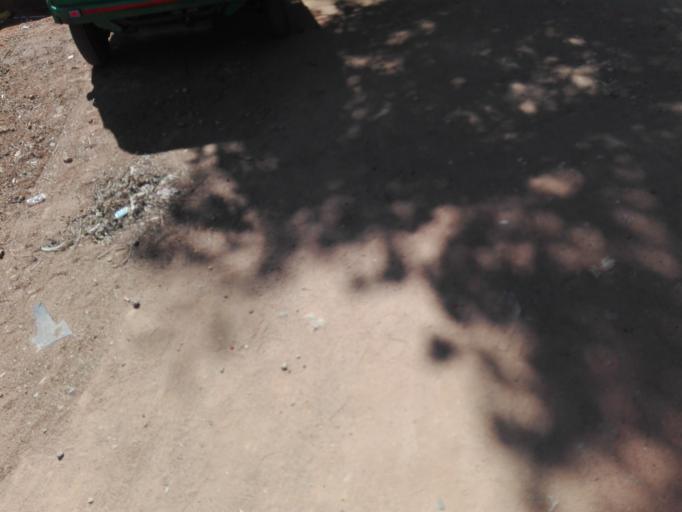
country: IN
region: Karnataka
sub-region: Bangalore Rural
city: Hoskote
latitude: 12.9816
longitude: 77.7279
